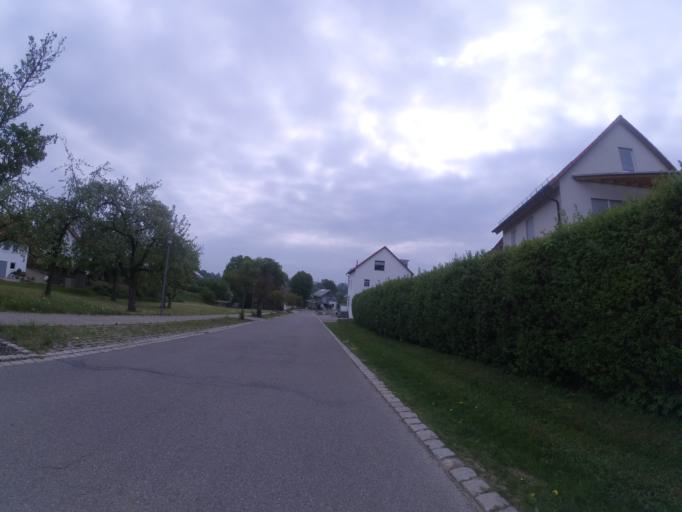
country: DE
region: Baden-Wuerttemberg
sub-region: Tuebingen Region
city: Staig
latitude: 48.3008
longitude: 9.9876
